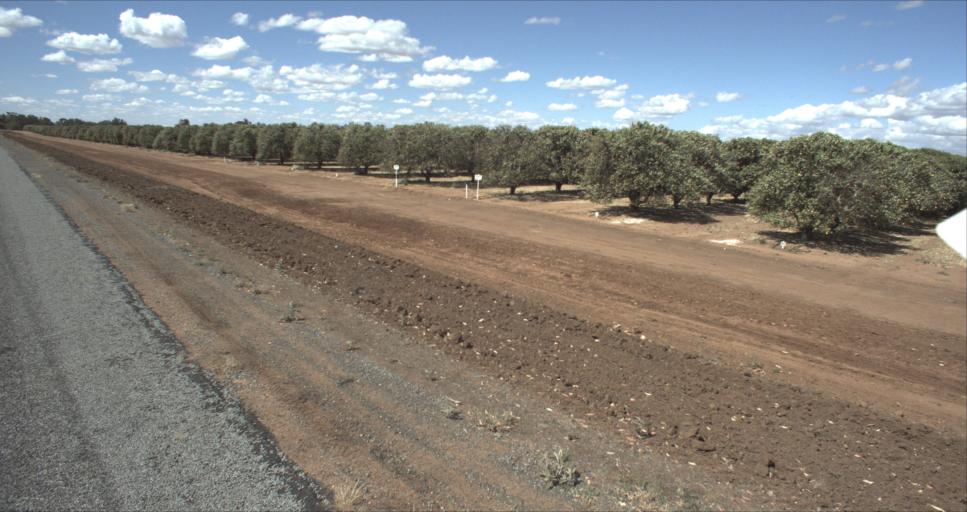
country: AU
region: New South Wales
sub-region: Leeton
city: Leeton
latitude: -34.5221
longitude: 146.2234
